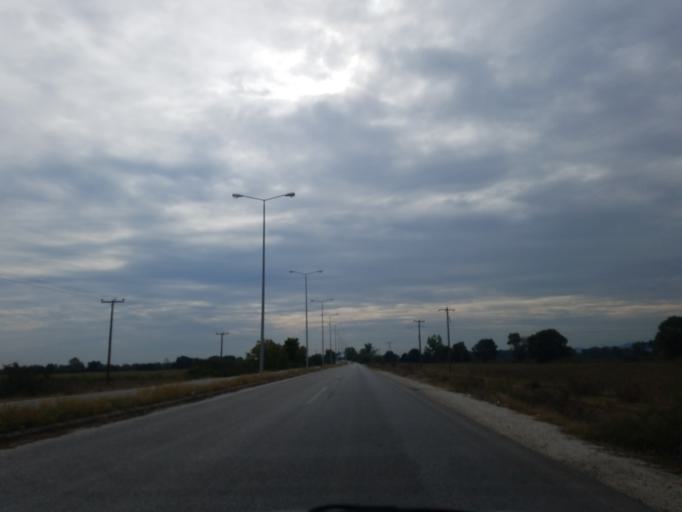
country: GR
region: Thessaly
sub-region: Trikala
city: Pyrgetos
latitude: 39.5252
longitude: 21.7496
